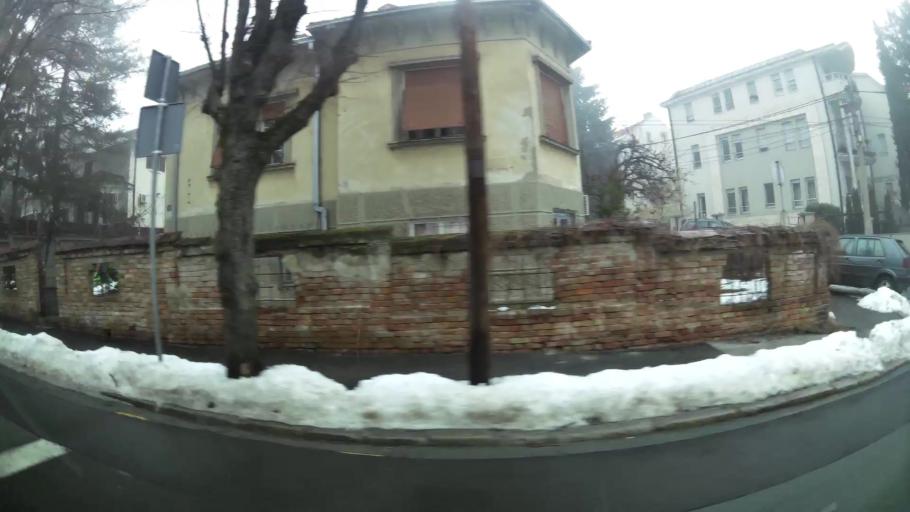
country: RS
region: Central Serbia
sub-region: Belgrade
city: Savski Venac
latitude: 44.7684
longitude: 20.4585
